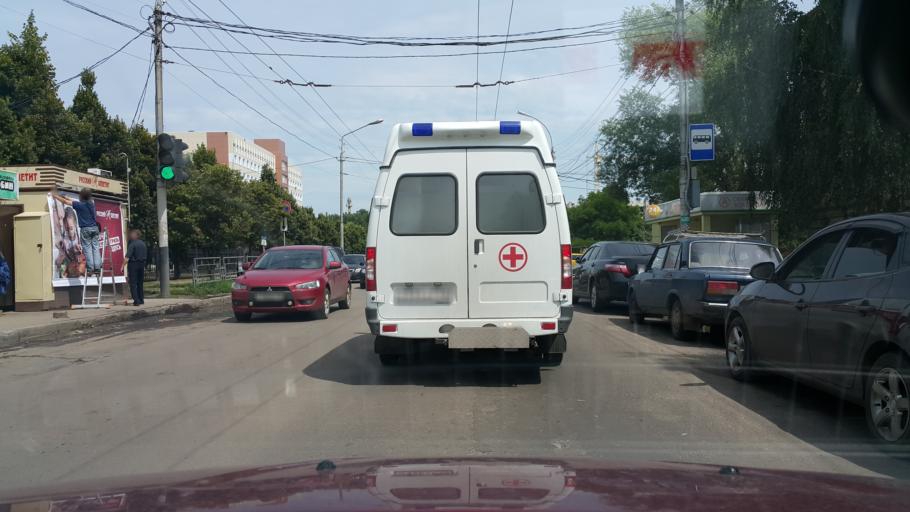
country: RU
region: Tambov
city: Tambov
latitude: 52.7319
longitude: 41.4682
